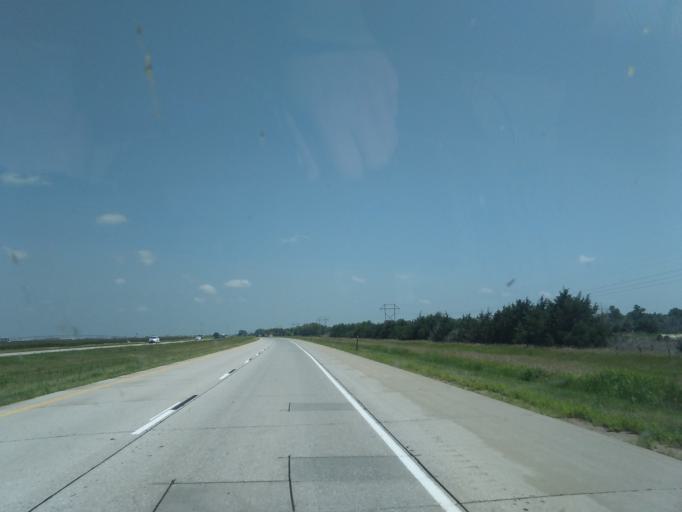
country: US
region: Nebraska
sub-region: Dawson County
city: Lexington
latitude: 40.7501
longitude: -99.7764
